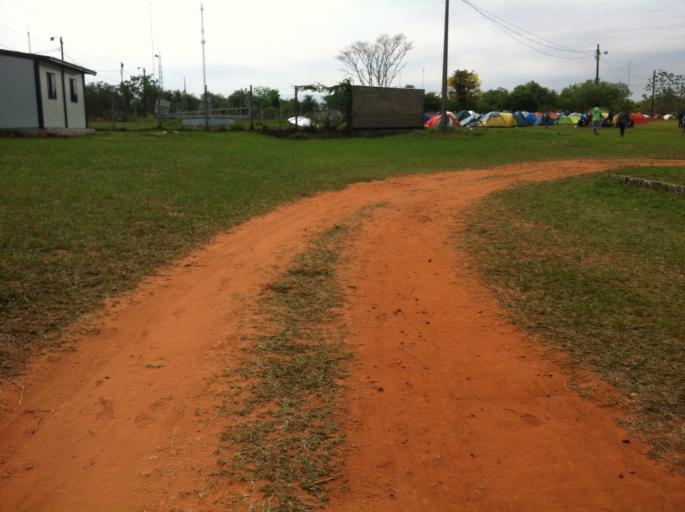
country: PY
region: Central
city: San Lorenzo
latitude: -25.2963
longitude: -57.4907
